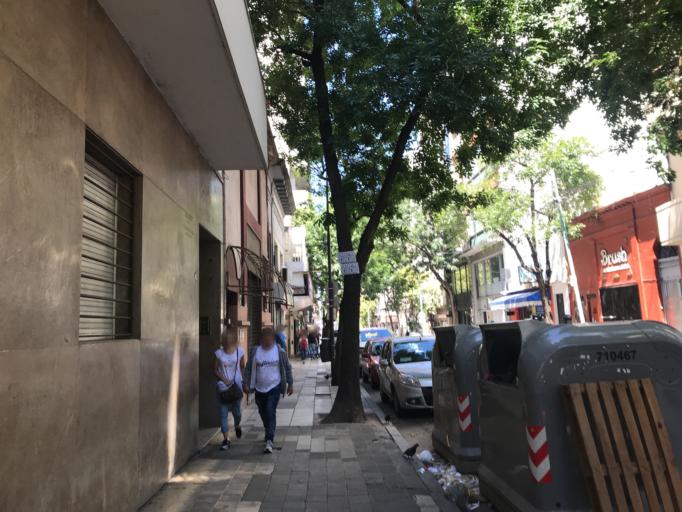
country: AR
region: Buenos Aires F.D.
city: Buenos Aires
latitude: -34.6023
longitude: -58.3985
